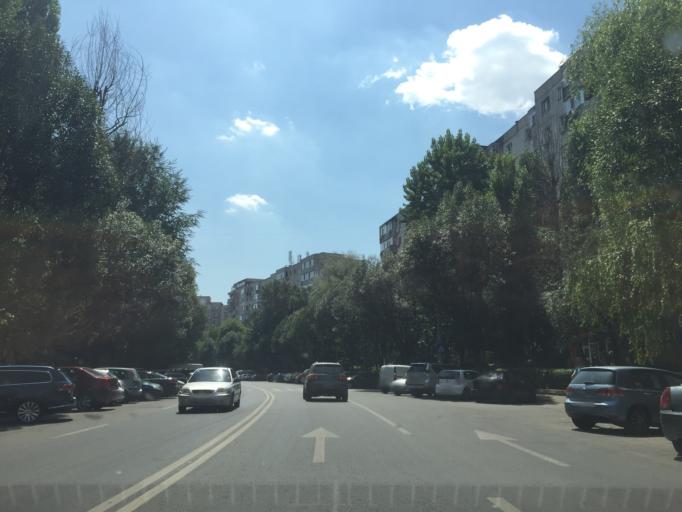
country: RO
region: Bucuresti
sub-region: Municipiul Bucuresti
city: Bucharest
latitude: 44.4115
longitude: 26.1147
